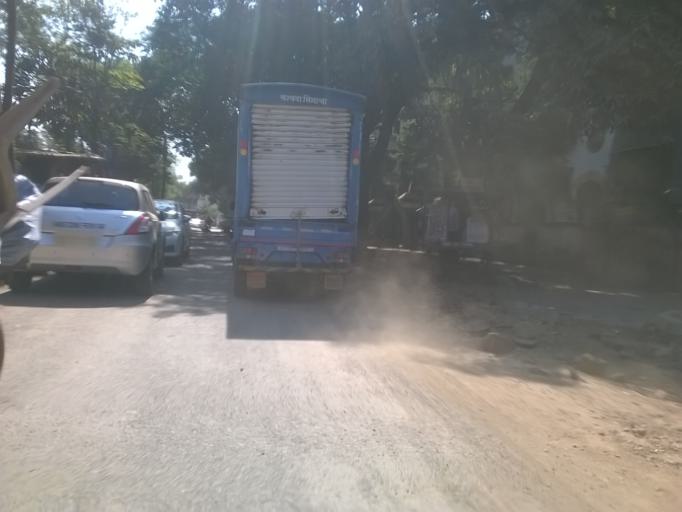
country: IN
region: Maharashtra
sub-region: Raigarh
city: Kalundri
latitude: 18.9919
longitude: 73.1258
